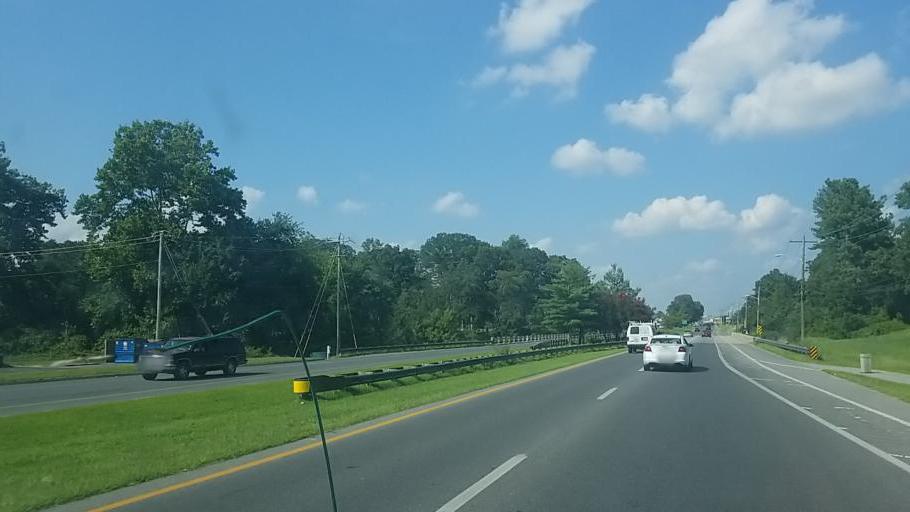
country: US
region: Maryland
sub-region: Wicomico County
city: Fruitland
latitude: 38.3323
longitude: -75.6114
